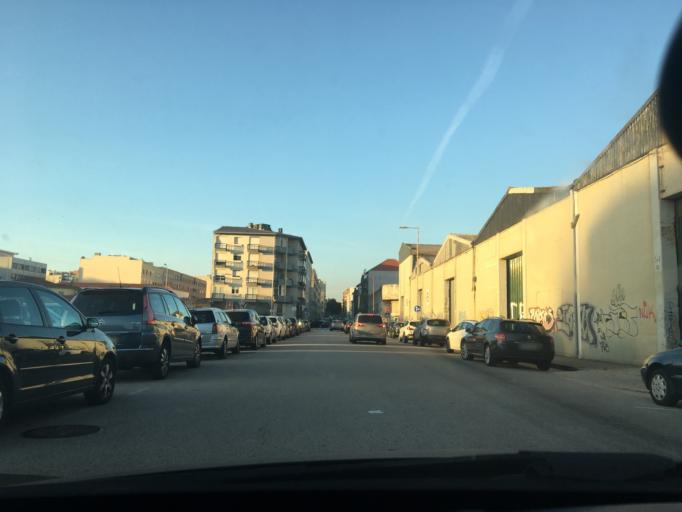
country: PT
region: Porto
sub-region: Matosinhos
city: Matosinhos
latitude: 41.1759
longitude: -8.6871
